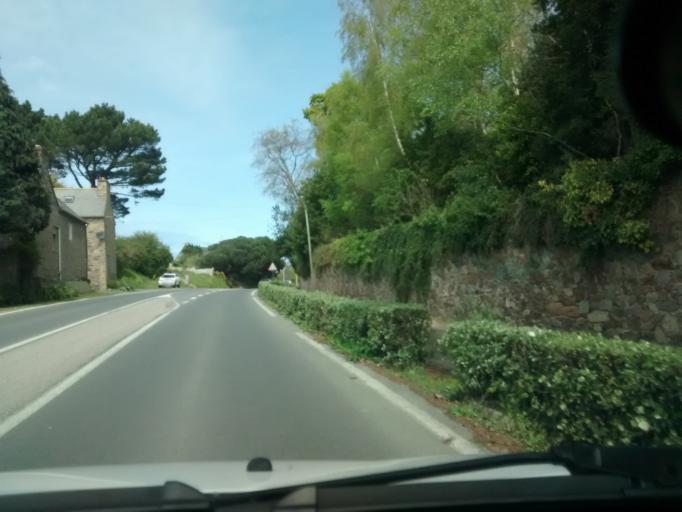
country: FR
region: Brittany
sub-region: Departement des Cotes-d'Armor
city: Paimpol
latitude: 48.7885
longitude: -3.0491
